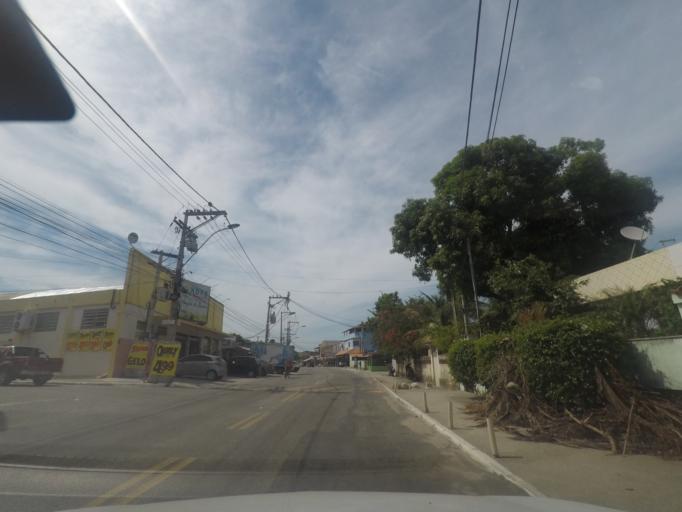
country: BR
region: Rio de Janeiro
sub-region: Marica
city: Marica
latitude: -22.9510
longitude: -42.6970
